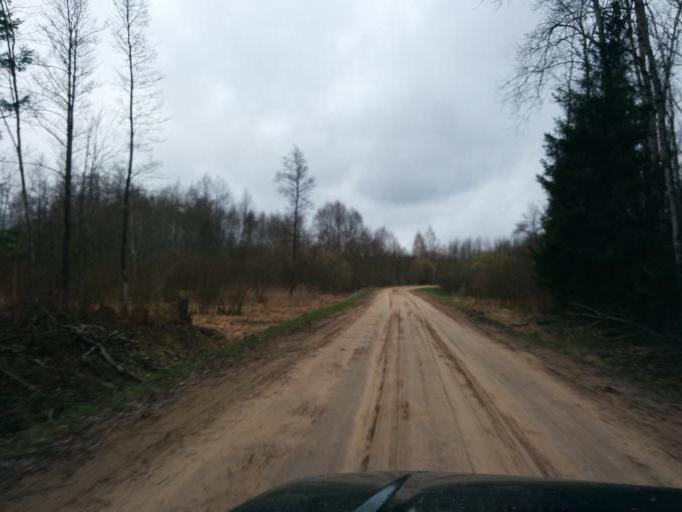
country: LV
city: Tireli
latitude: 56.7859
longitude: 23.6453
